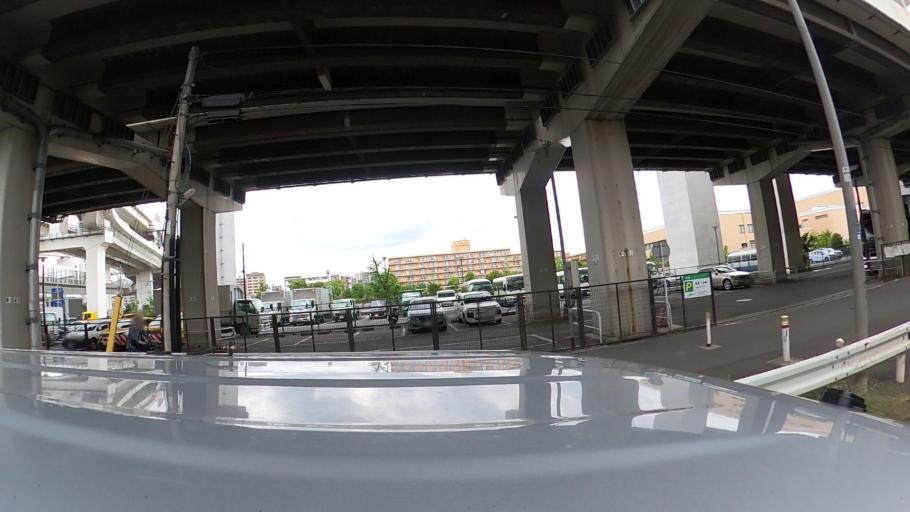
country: JP
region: Kanagawa
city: Yokohama
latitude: 35.4919
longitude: 139.6716
